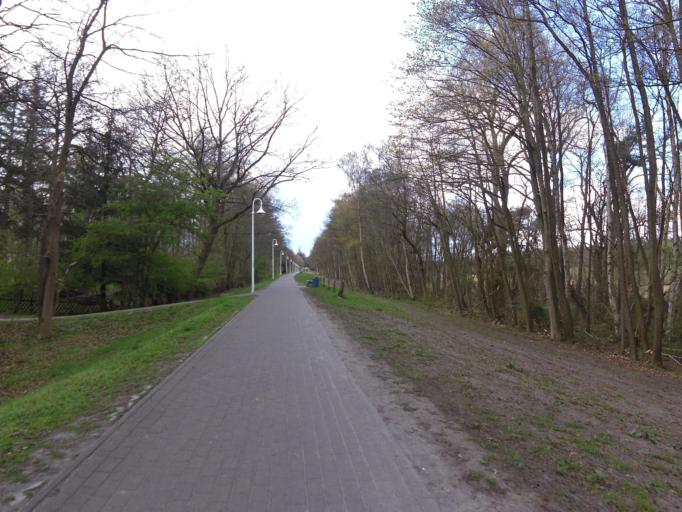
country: DE
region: Mecklenburg-Vorpommern
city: Ostseebad Prerow
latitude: 54.4483
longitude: 12.5745
